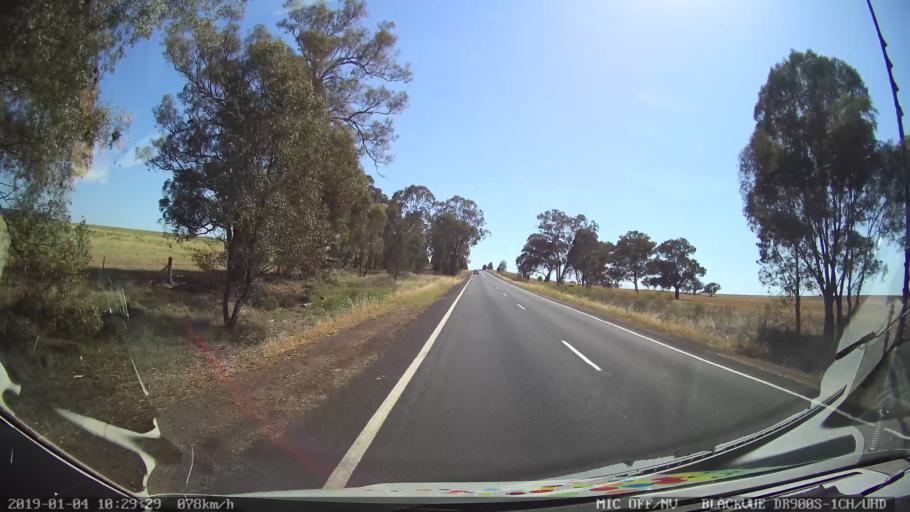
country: AU
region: New South Wales
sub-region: Cabonne
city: Canowindra
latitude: -33.3551
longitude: 148.6207
